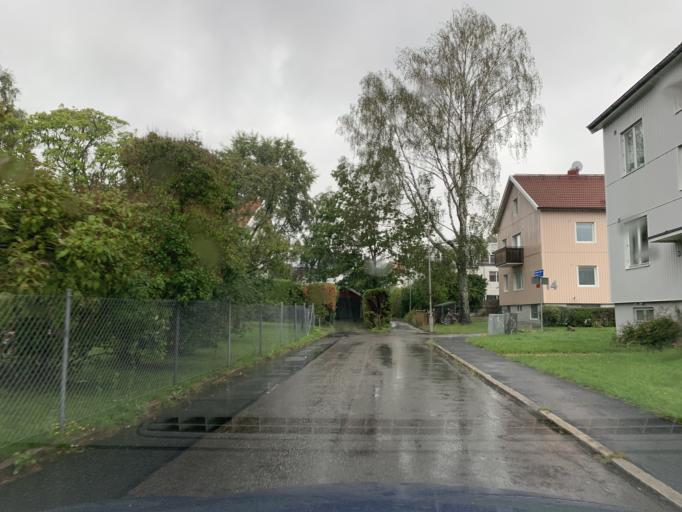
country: SE
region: Vaestra Goetaland
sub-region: Goteborg
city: Goeteborg
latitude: 57.7114
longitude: 12.0204
